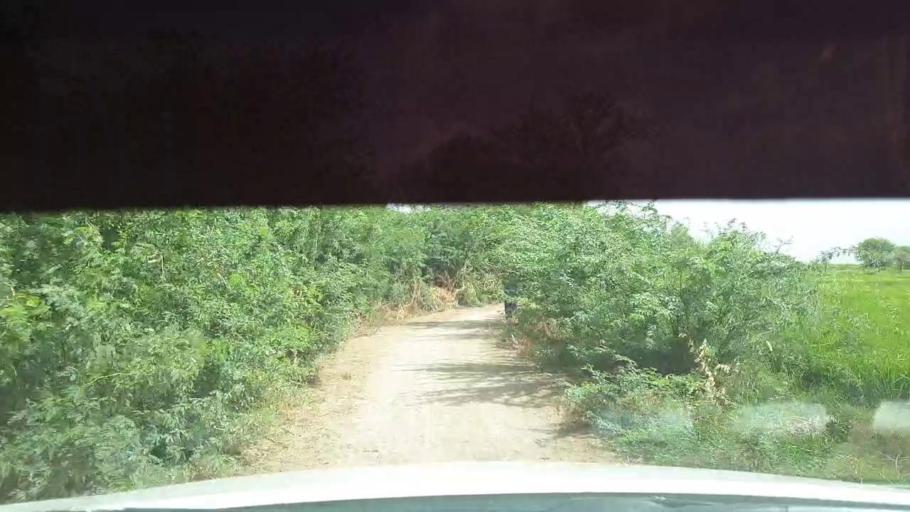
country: PK
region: Sindh
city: Kadhan
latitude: 24.6134
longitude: 69.0260
